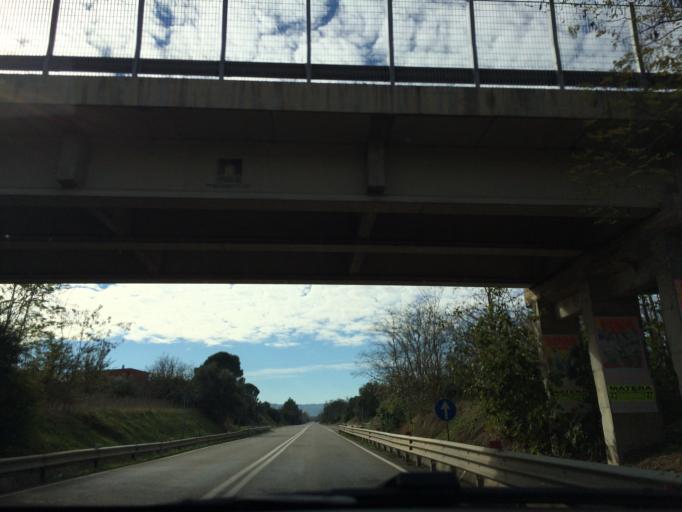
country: IT
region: Basilicate
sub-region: Provincia di Matera
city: Matera
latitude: 40.6109
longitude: 16.5740
